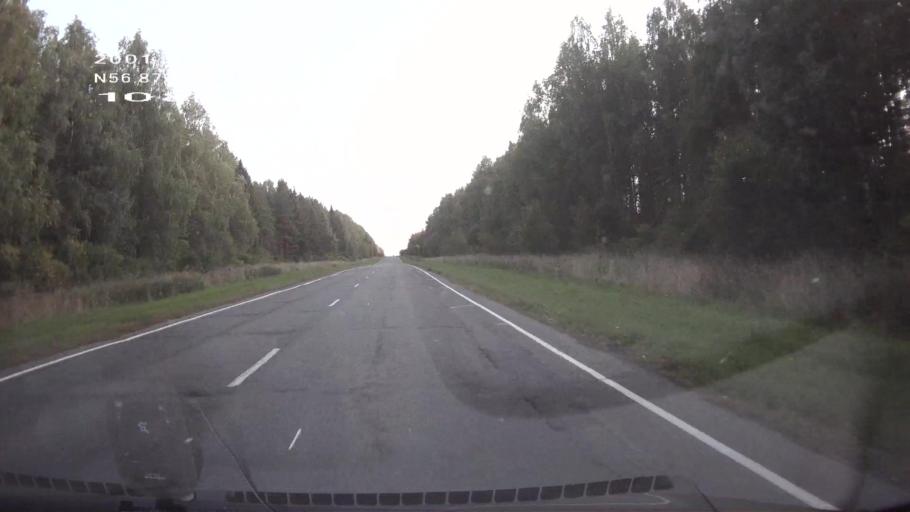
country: RU
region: Mariy-El
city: Kuzhener
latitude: 56.8779
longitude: 48.7537
